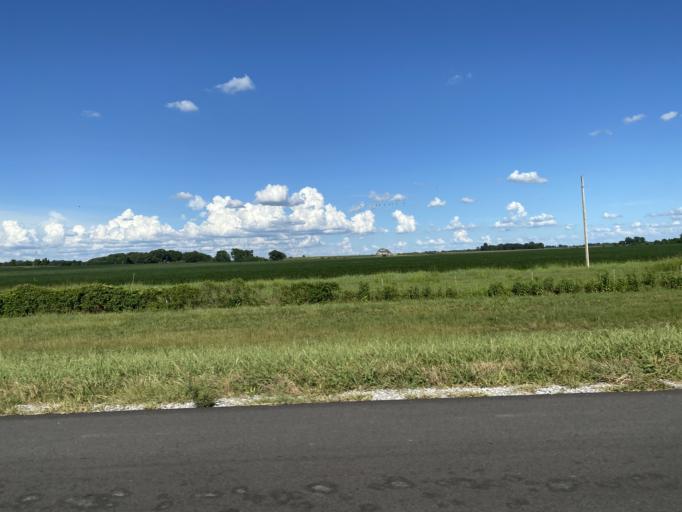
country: US
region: Alabama
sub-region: Limestone County
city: Athens
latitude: 34.7419
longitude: -86.9385
